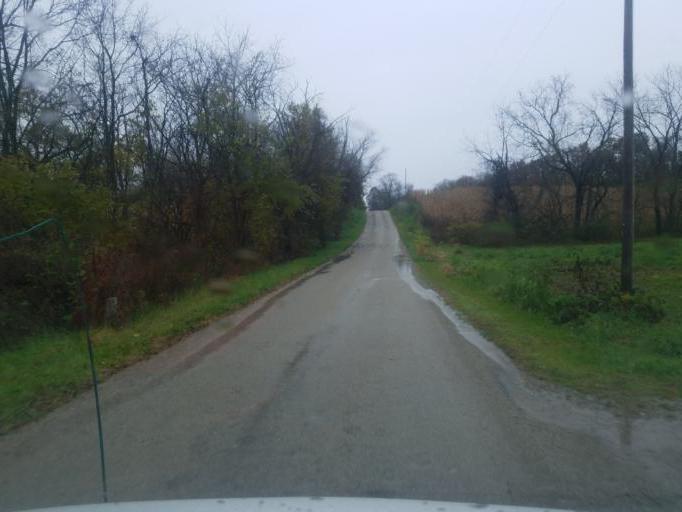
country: US
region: Ohio
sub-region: Washington County
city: Beverly
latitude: 39.4713
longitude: -81.6960
